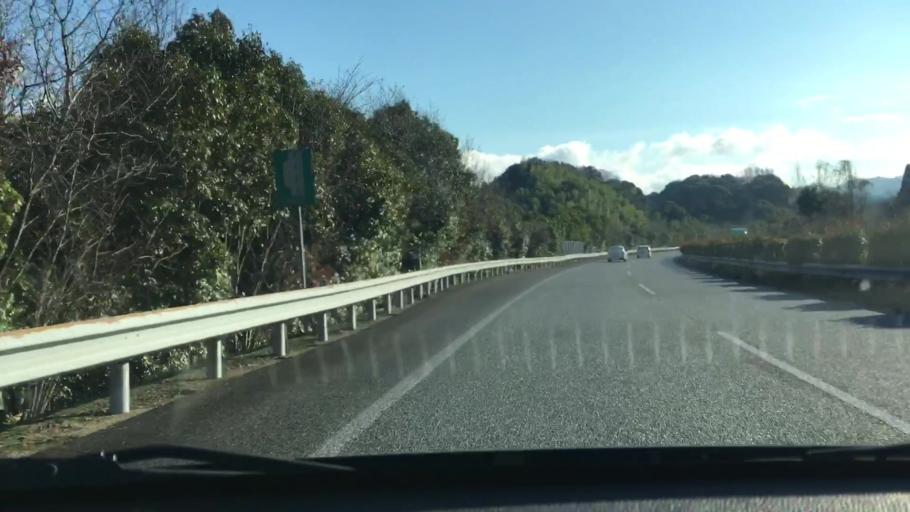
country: JP
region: Kumamoto
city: Hitoyoshi
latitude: 32.1960
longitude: 130.7778
